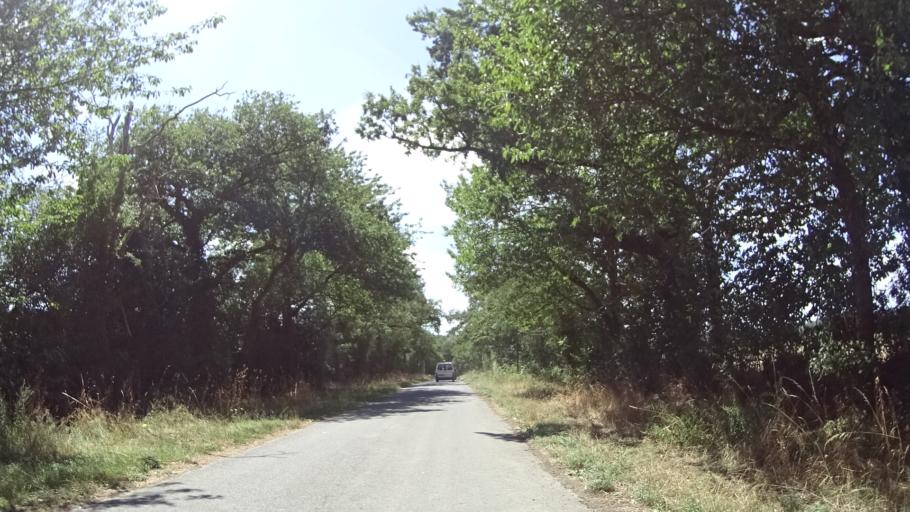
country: FR
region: Pays de la Loire
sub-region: Departement de Maine-et-Loire
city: Cande
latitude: 47.6145
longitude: -0.9970
